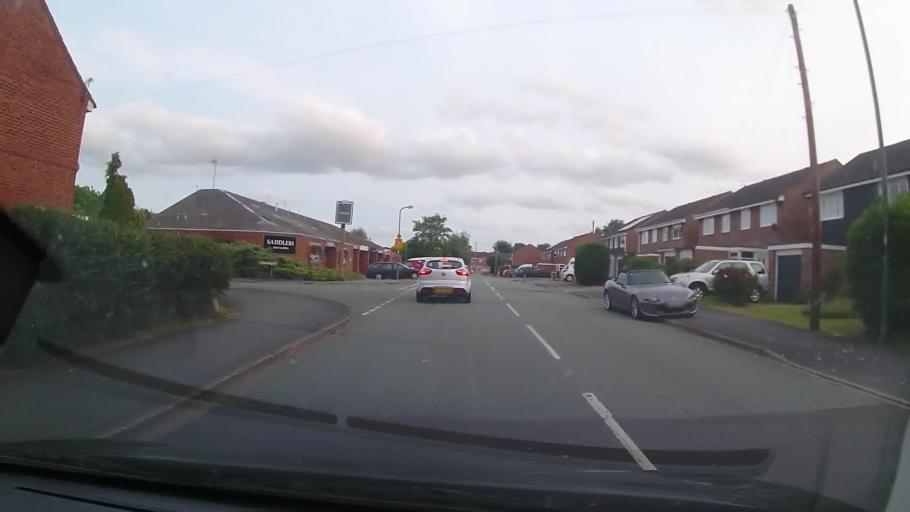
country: GB
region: England
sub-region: Shropshire
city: Shrewsbury
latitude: 52.6960
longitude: -2.7398
